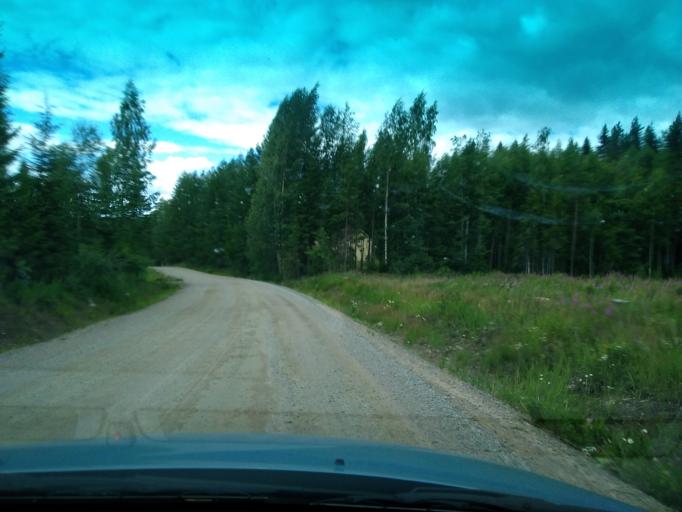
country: FI
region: Central Finland
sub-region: Saarijaervi-Viitasaari
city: Karstula
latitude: 62.8090
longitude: 25.0108
